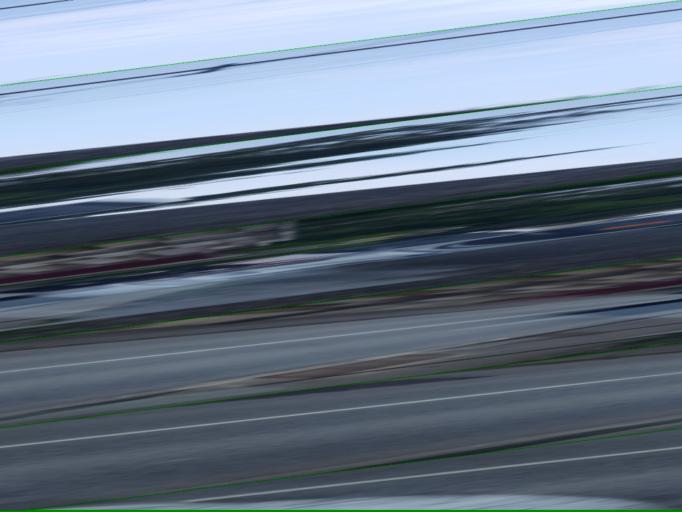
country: FR
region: Ile-de-France
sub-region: Departement des Yvelines
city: Septeuil
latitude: 48.9125
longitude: 1.6770
